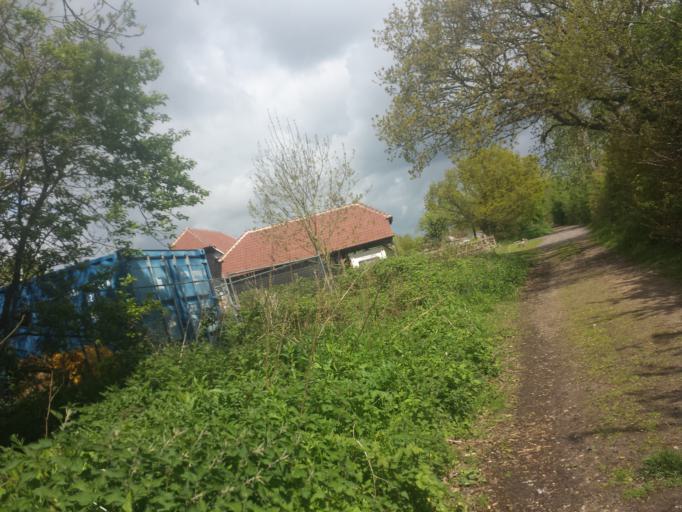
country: GB
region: England
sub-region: Essex
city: Great Bentley
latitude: 51.8806
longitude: 1.0446
